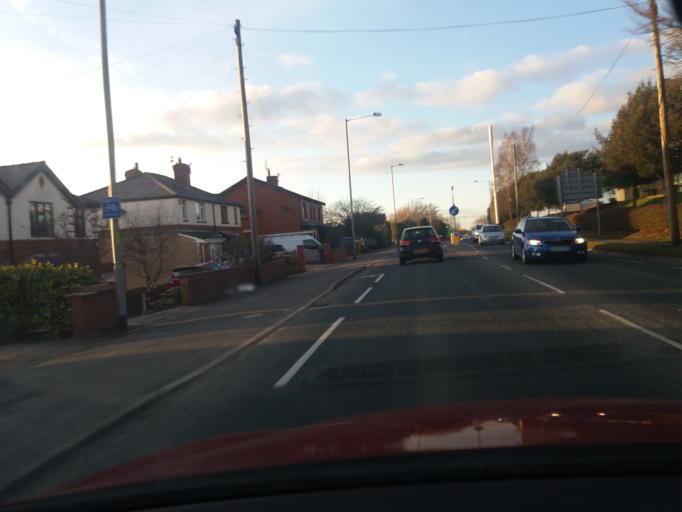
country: GB
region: England
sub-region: Lancashire
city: Chorley
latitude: 53.6745
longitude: -2.6348
